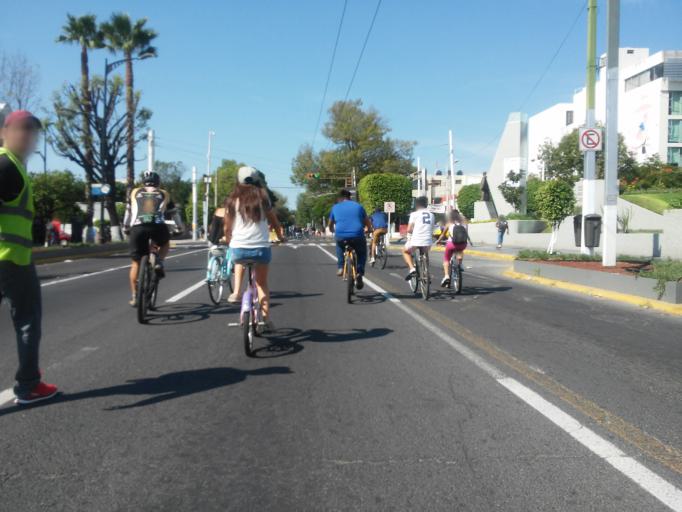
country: MX
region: Jalisco
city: Guadalajara
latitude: 20.6748
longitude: -103.3589
